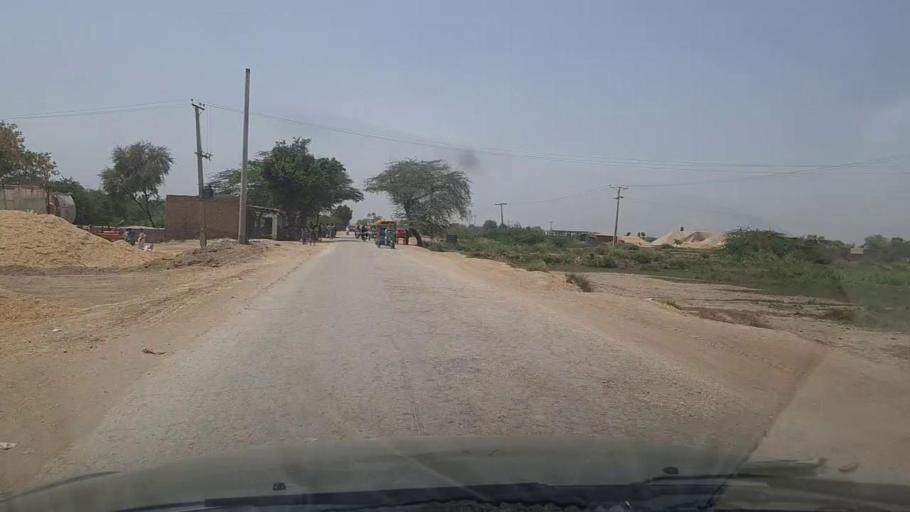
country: PK
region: Sindh
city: Bhiria
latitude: 26.8830
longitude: 68.2963
